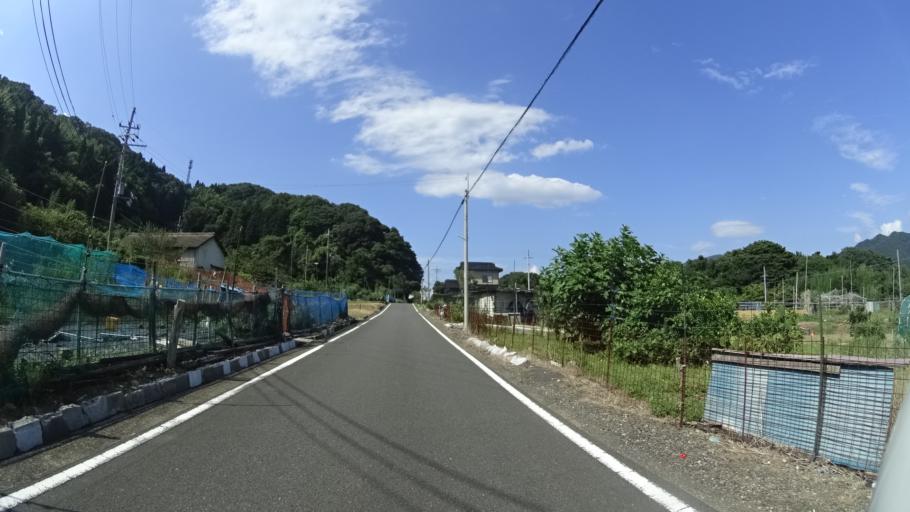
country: JP
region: Kyoto
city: Maizuru
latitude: 35.5043
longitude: 135.3332
